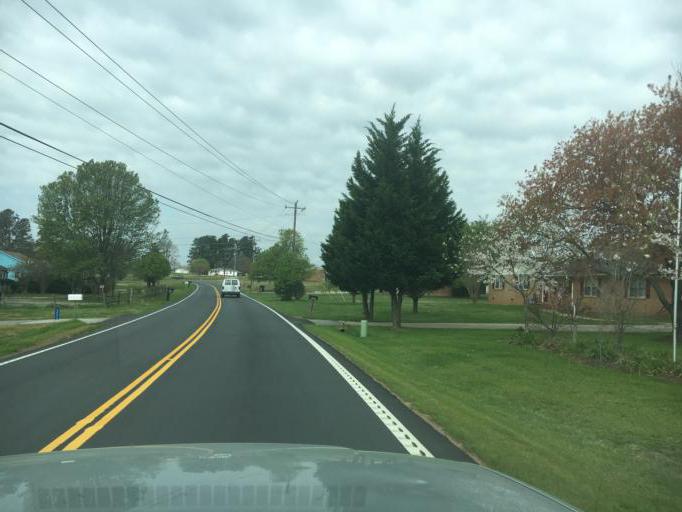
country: US
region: South Carolina
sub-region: Spartanburg County
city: Inman Mills
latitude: 35.0577
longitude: -82.1488
